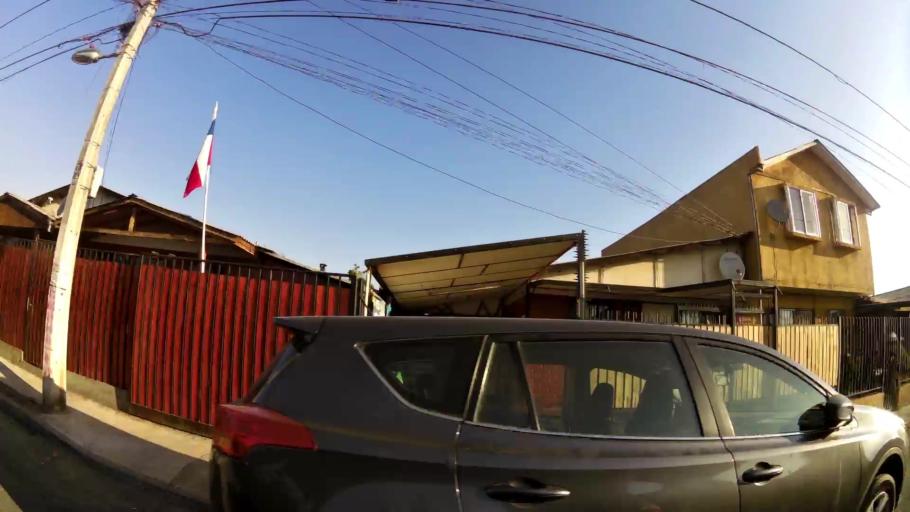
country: CL
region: Santiago Metropolitan
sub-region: Provincia de Santiago
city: La Pintana
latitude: -33.5488
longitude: -70.6213
